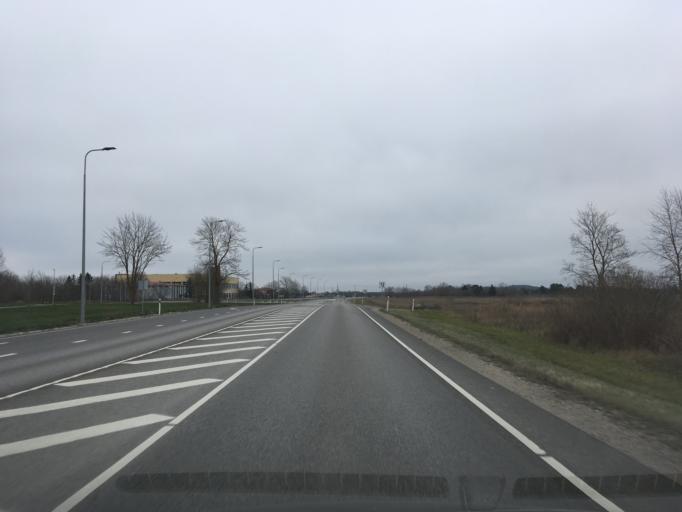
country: EE
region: Ida-Virumaa
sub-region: Sillamaee linn
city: Sillamae
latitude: 59.3892
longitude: 27.7930
